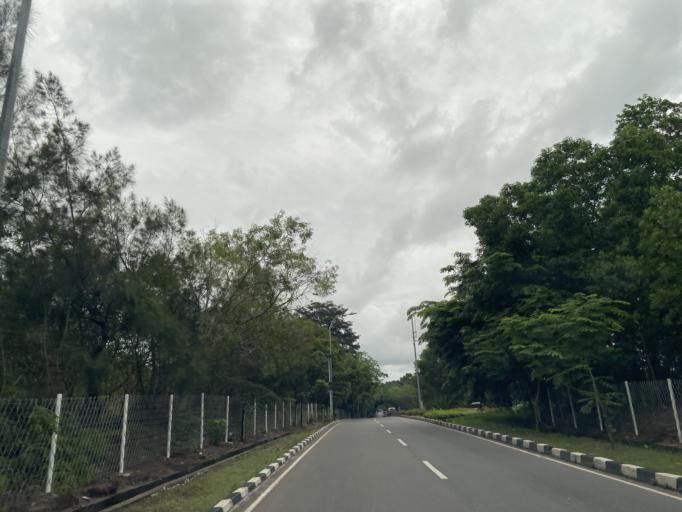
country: SG
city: Singapore
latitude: 1.1081
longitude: 104.0053
